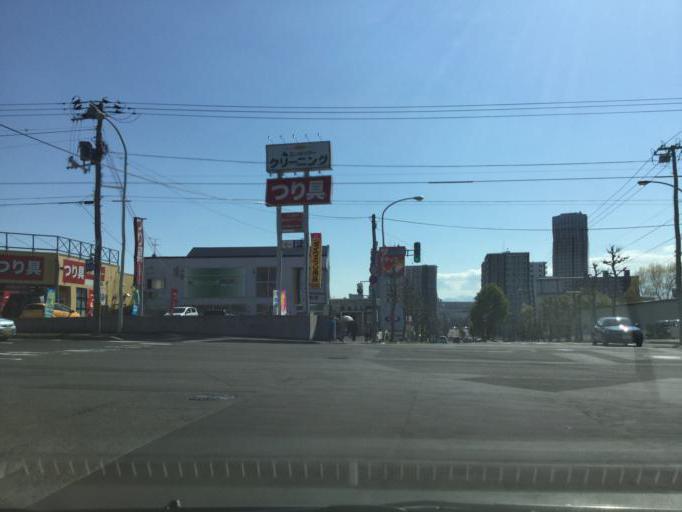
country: JP
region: Hokkaido
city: Ebetsu
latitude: 43.0430
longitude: 141.4807
